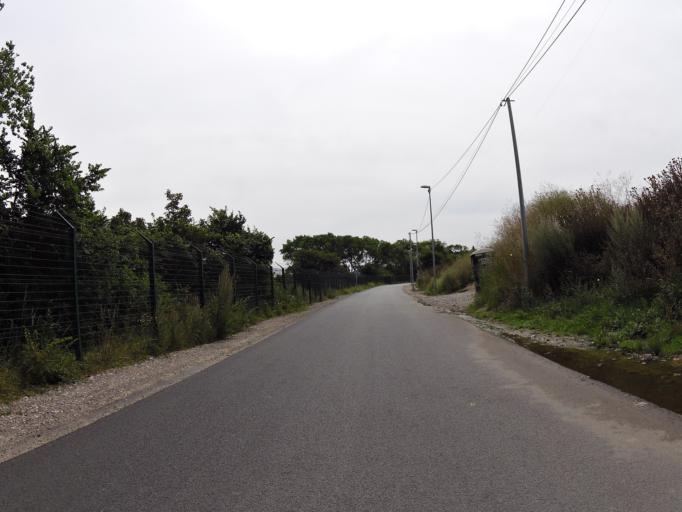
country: FR
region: Nord-Pas-de-Calais
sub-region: Departement du Pas-de-Calais
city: Marck
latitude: 50.9697
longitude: 1.9094
